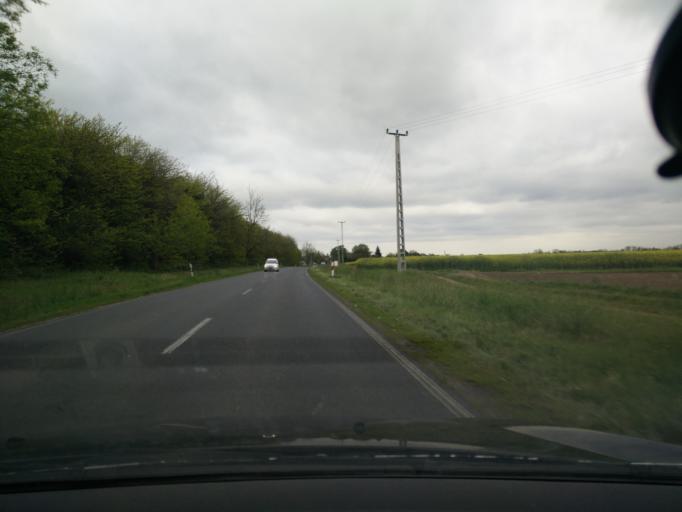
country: HU
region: Veszprem
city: Papa
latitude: 47.3864
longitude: 17.4710
